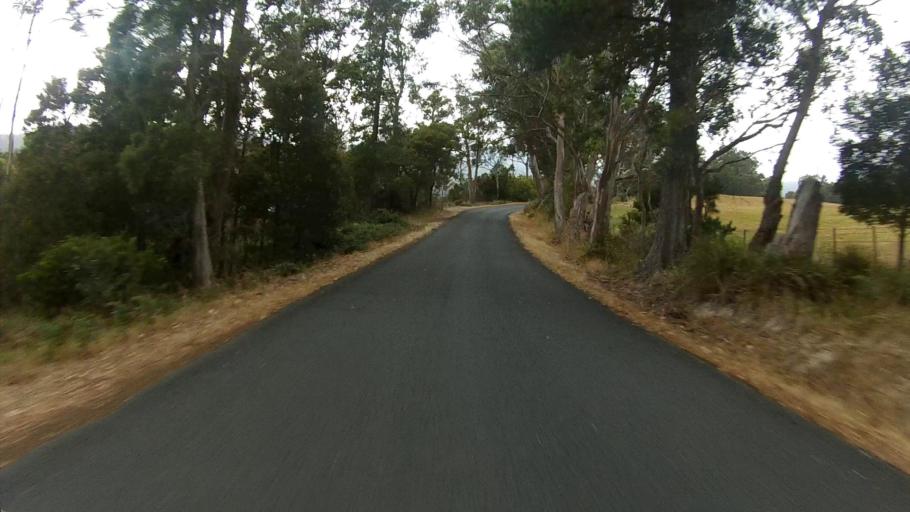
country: AU
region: Tasmania
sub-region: Huon Valley
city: Cygnet
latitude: -43.2145
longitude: 147.1074
